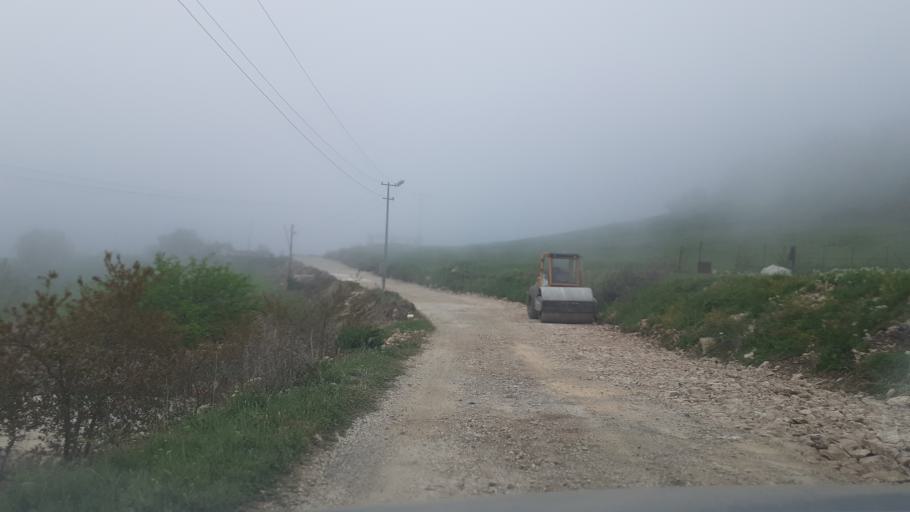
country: TR
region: Hatay
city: Yeditepe
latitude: 35.9713
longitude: 36.0028
